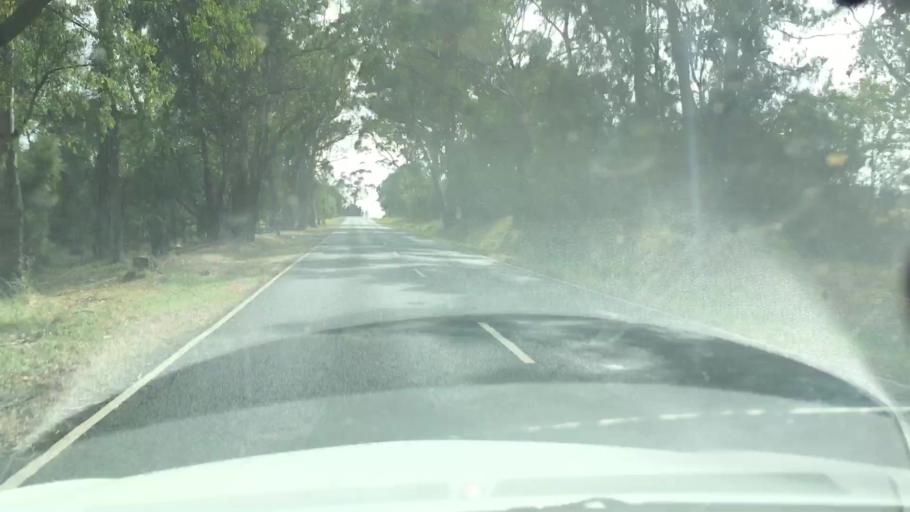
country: AU
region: Victoria
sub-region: Yarra Ranges
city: Woori Yallock
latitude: -37.8072
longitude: 145.5158
